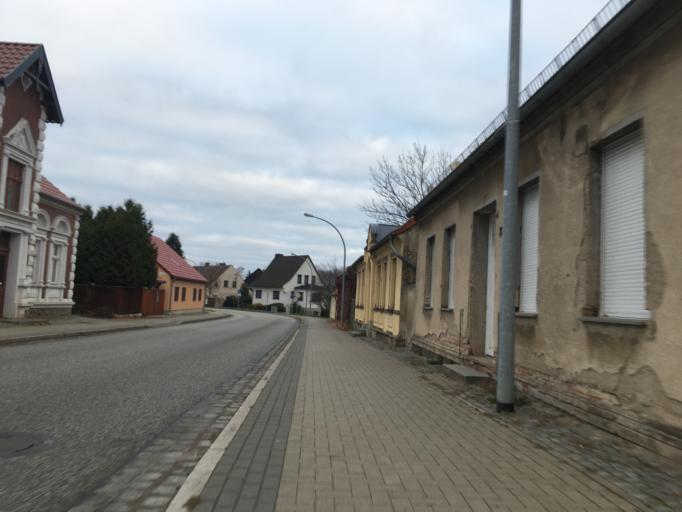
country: DE
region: Brandenburg
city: Seelow
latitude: 52.5724
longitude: 14.3543
